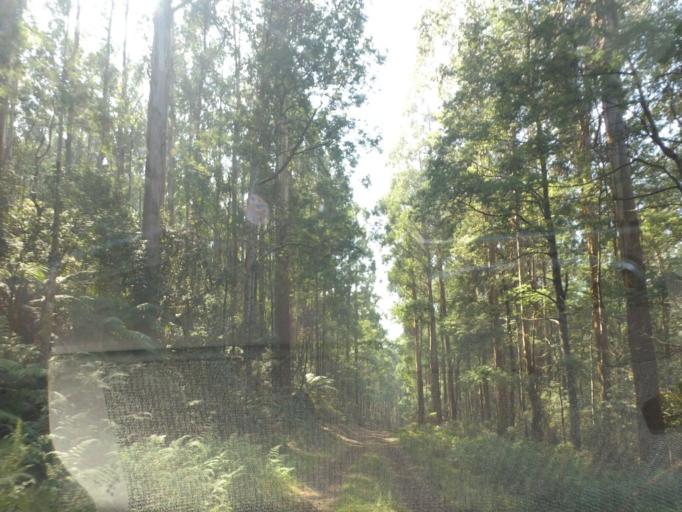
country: AU
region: Victoria
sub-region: Yarra Ranges
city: Healesville
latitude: -37.5613
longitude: 145.6068
